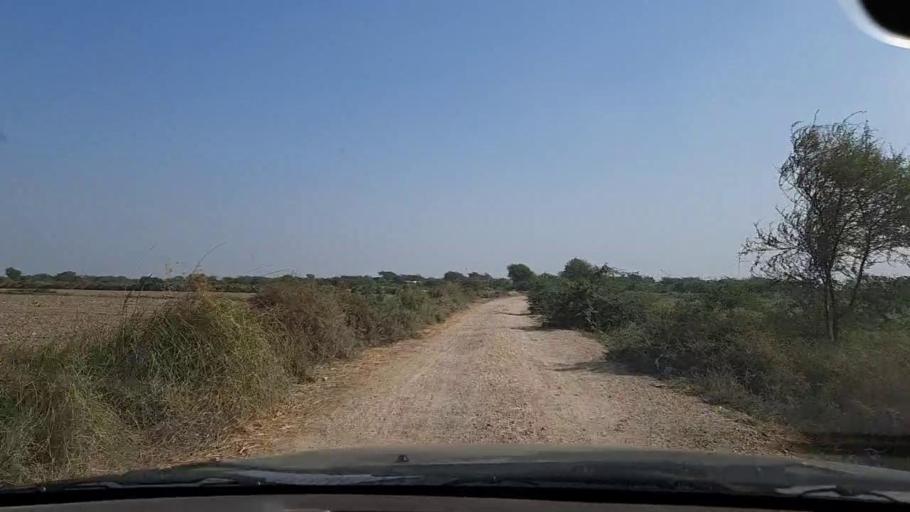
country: PK
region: Sindh
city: Chuhar Jamali
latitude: 24.4180
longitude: 67.8312
